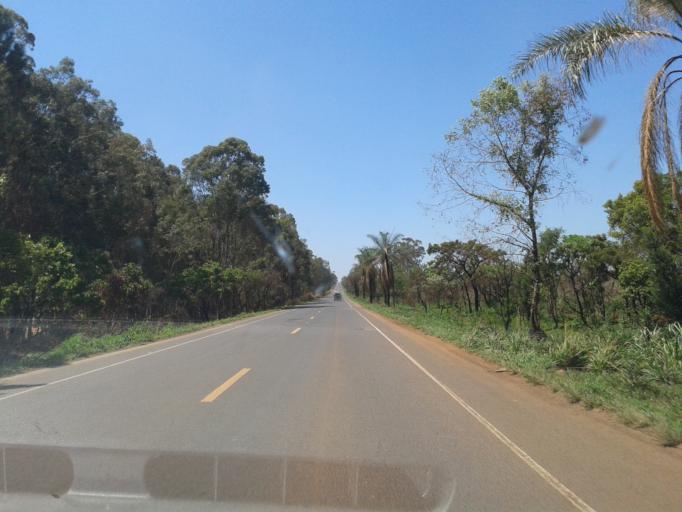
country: BR
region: Minas Gerais
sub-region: Araxa
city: Araxa
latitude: -19.3899
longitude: -47.3366
